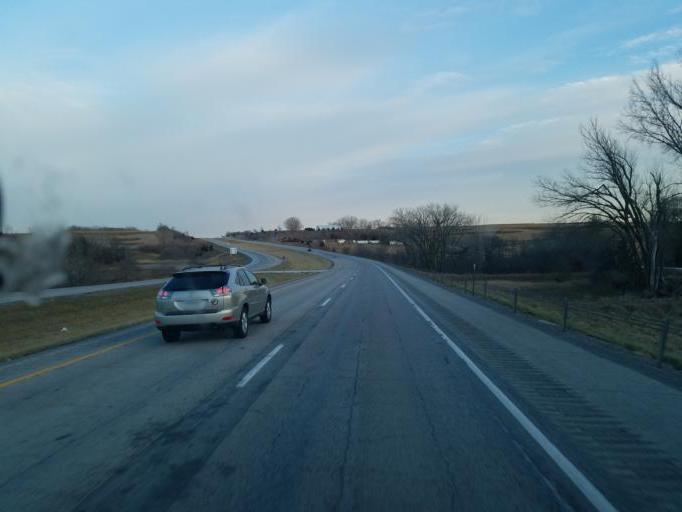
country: US
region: Iowa
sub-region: Harrison County
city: Missouri Valley
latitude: 41.4935
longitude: -95.8569
